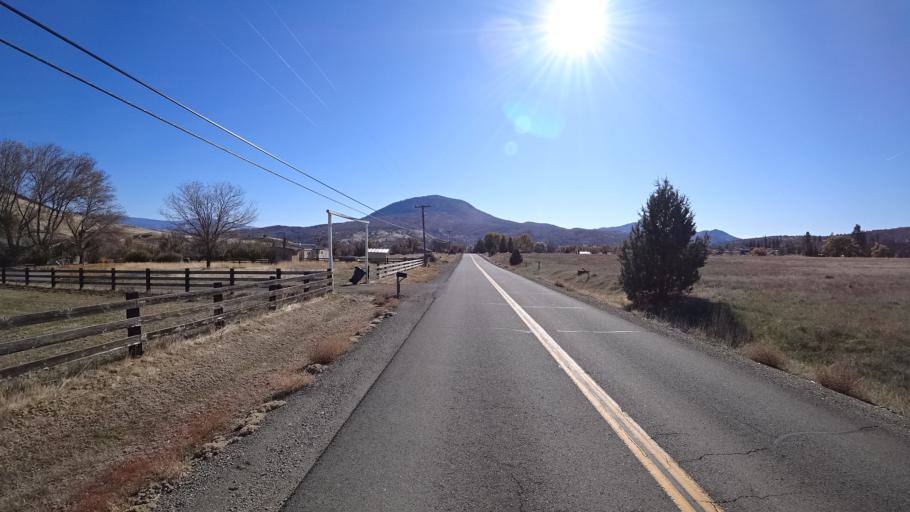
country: US
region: California
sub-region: Siskiyou County
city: Montague
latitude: 41.9052
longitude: -122.5554
